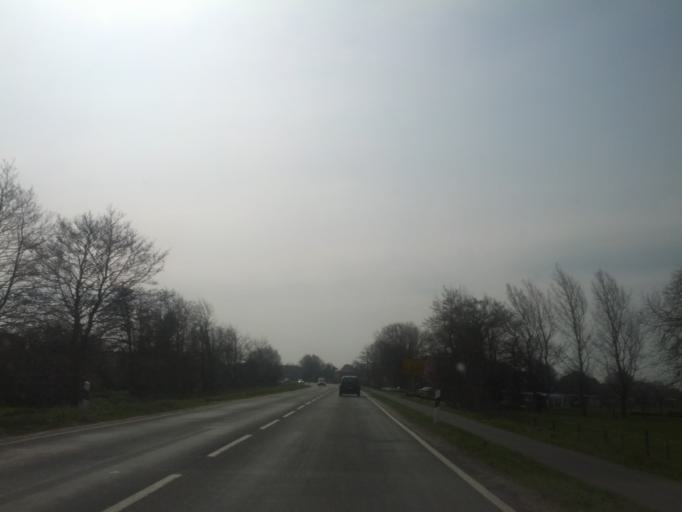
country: DE
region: Lower Saxony
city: Osteel
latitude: 53.5499
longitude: 7.2549
